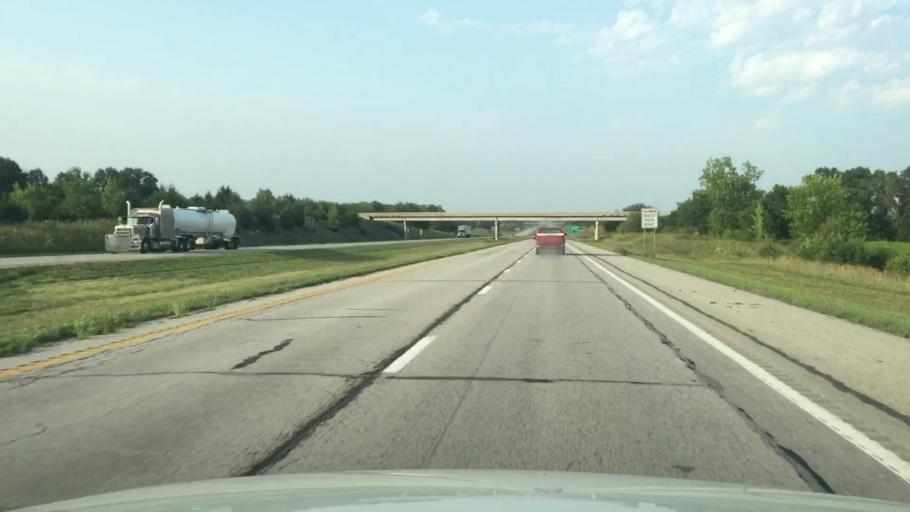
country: US
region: Missouri
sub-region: Harrison County
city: Bethany
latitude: 40.1359
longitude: -94.0470
